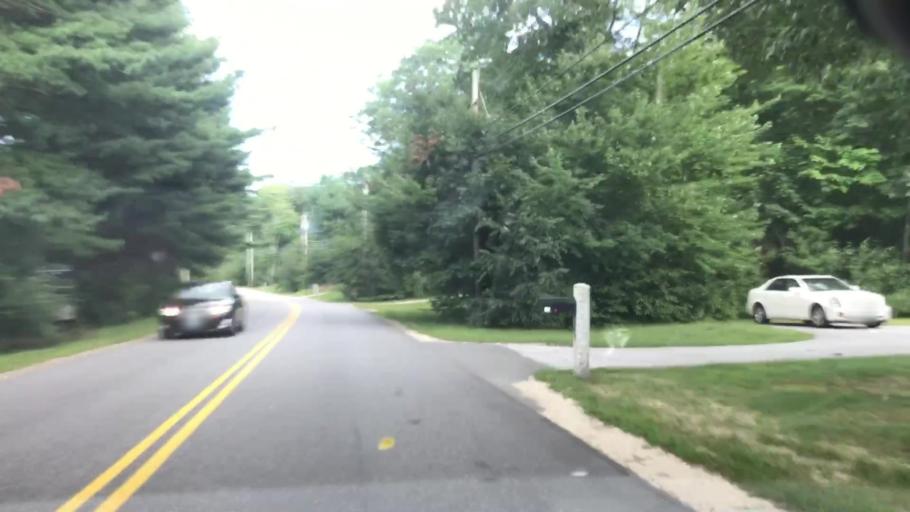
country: US
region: New Hampshire
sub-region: Hillsborough County
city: Milford
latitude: 42.8194
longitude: -71.5857
